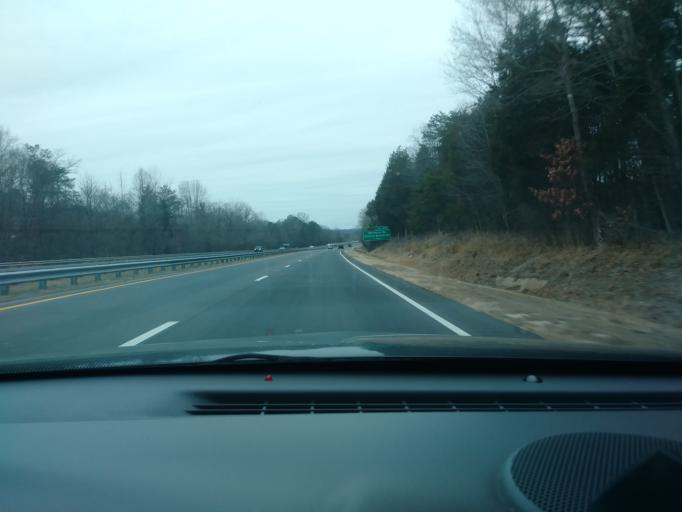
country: US
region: North Carolina
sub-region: Forsyth County
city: Lewisville
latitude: 36.1020
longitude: -80.5003
